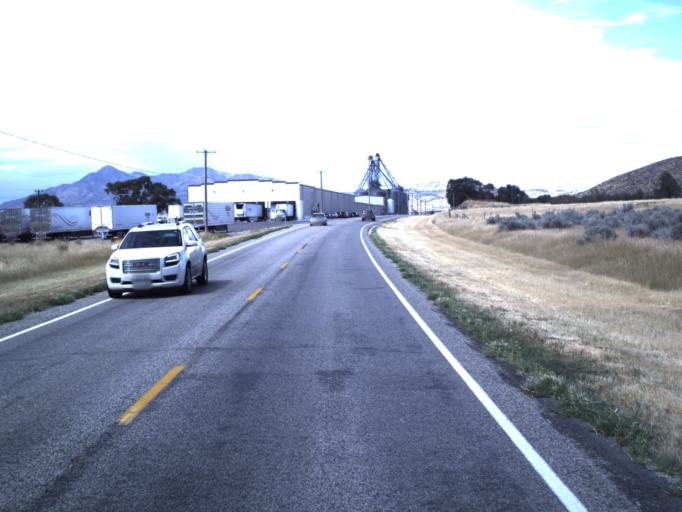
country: US
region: Utah
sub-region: Box Elder County
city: Garland
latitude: 41.7702
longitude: -112.0967
